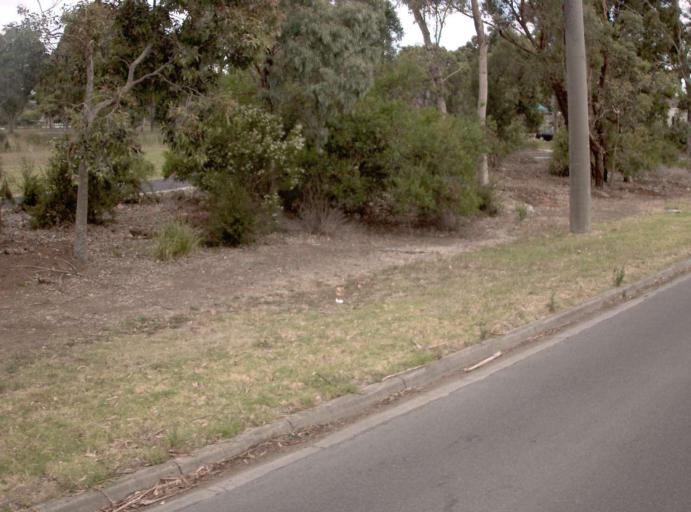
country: AU
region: Victoria
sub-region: Knox
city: Scoresby
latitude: -37.9118
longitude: 145.2363
